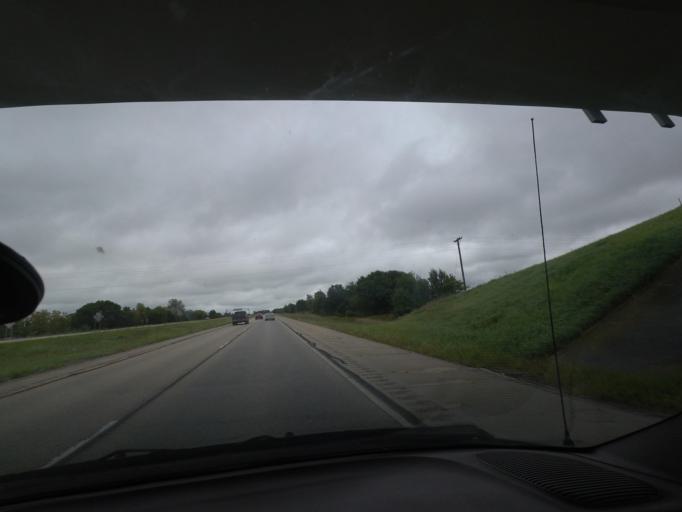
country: US
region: Illinois
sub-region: Piatt County
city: Cerro Gordo
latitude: 40.0181
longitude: -88.7257
